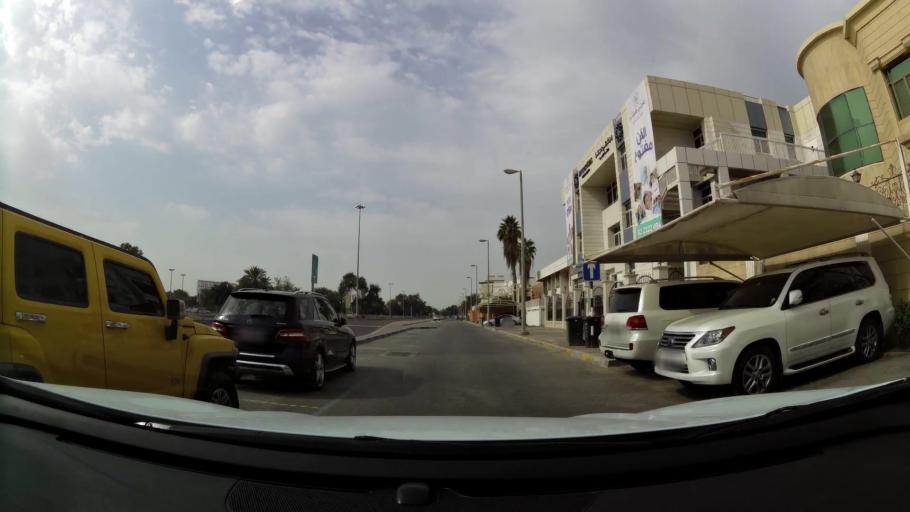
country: AE
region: Abu Dhabi
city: Abu Dhabi
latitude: 24.4571
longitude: 54.3811
